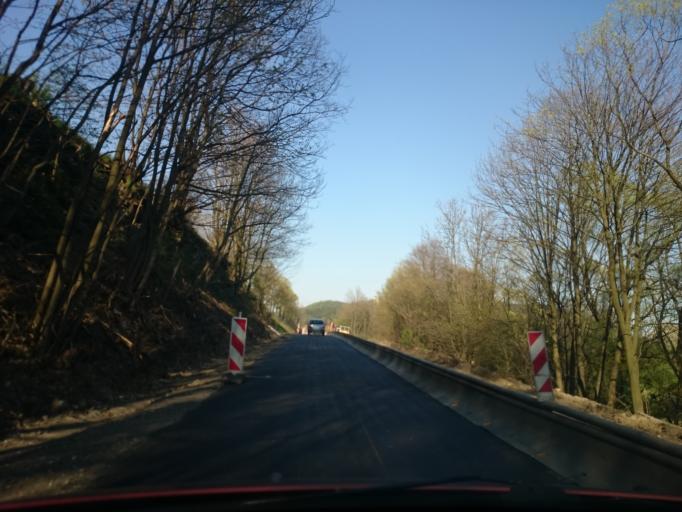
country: PL
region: Lower Silesian Voivodeship
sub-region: Powiat klodzki
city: Szczytna
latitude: 50.4101
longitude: 16.4376
